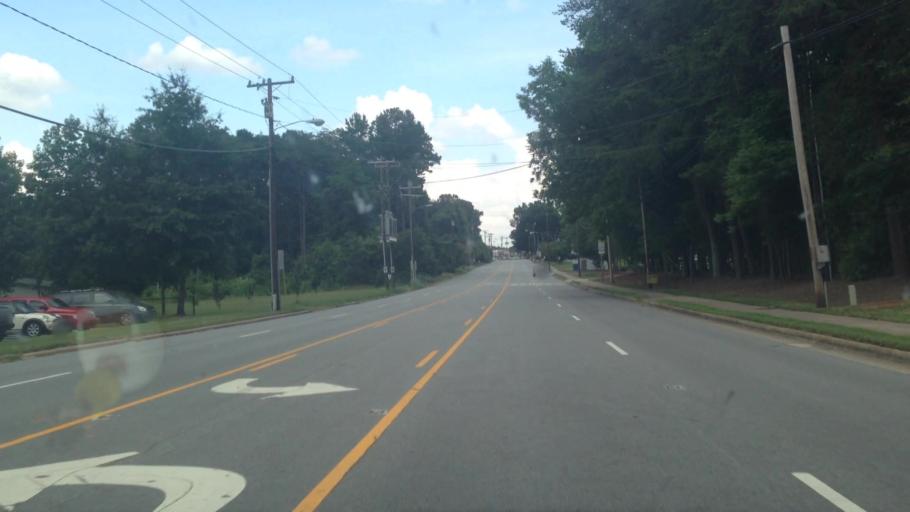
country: US
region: North Carolina
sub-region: Rockingham County
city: Mayodan
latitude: 36.4009
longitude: -79.9741
